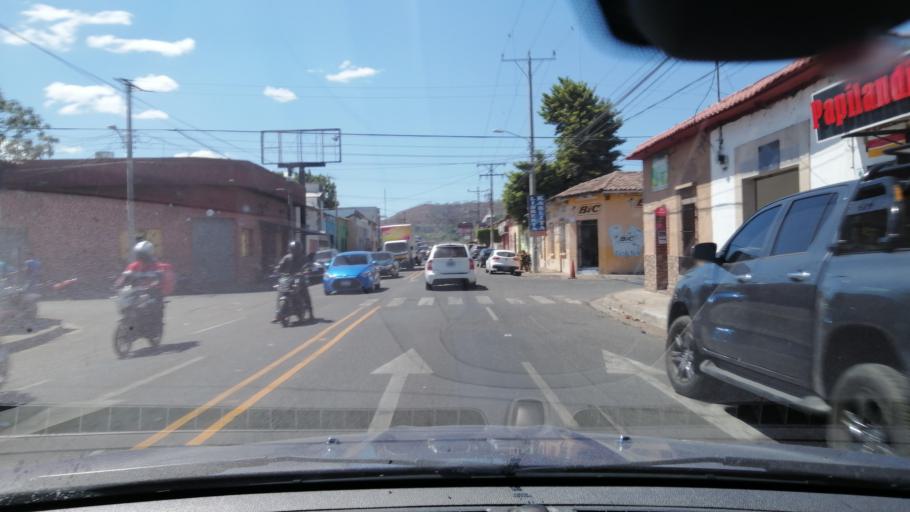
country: SV
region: Santa Ana
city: Santa Ana
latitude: 13.9824
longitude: -89.5598
